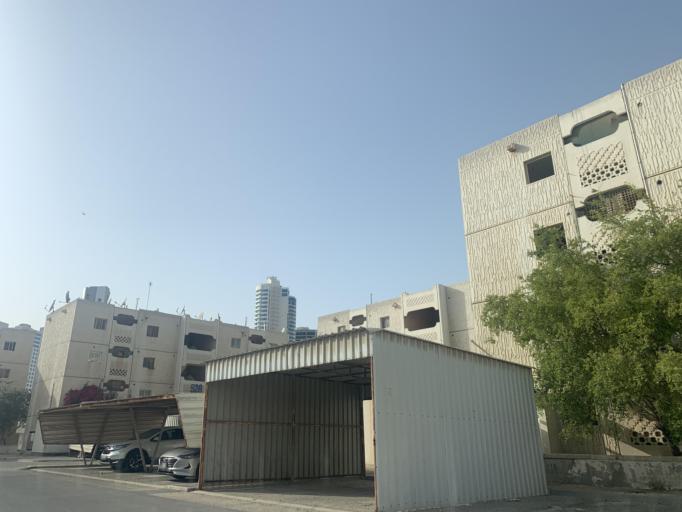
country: BH
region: Manama
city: Jidd Hafs
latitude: 26.2260
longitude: 50.5510
